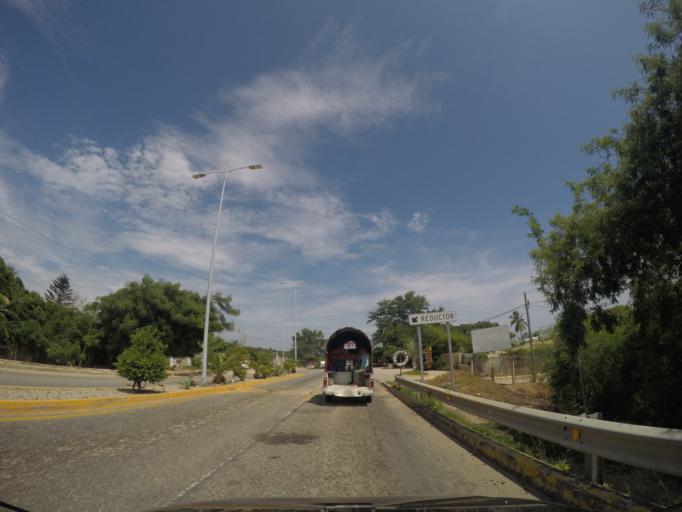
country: MX
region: Oaxaca
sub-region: Santa Maria Colotepec
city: Brisas de Zicatela
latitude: 15.8451
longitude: -97.0461
